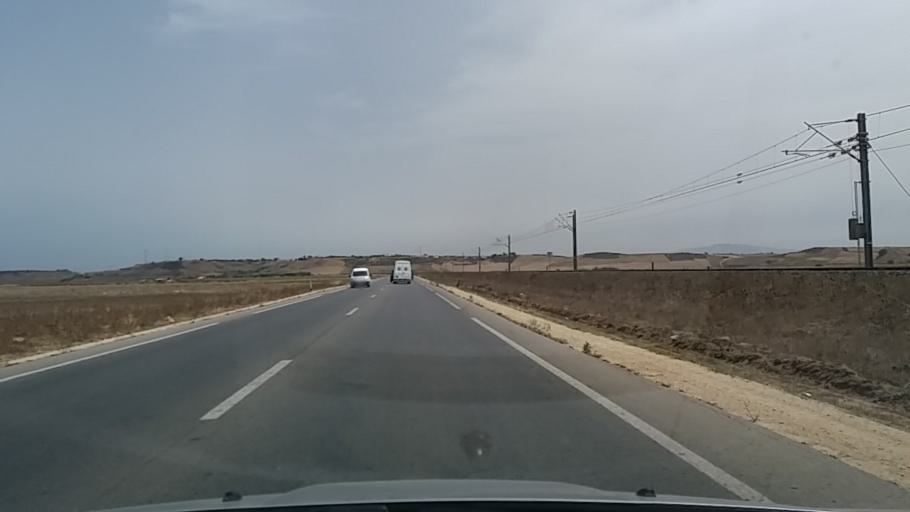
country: MA
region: Tanger-Tetouan
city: Asilah
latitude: 35.5004
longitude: -6.0091
